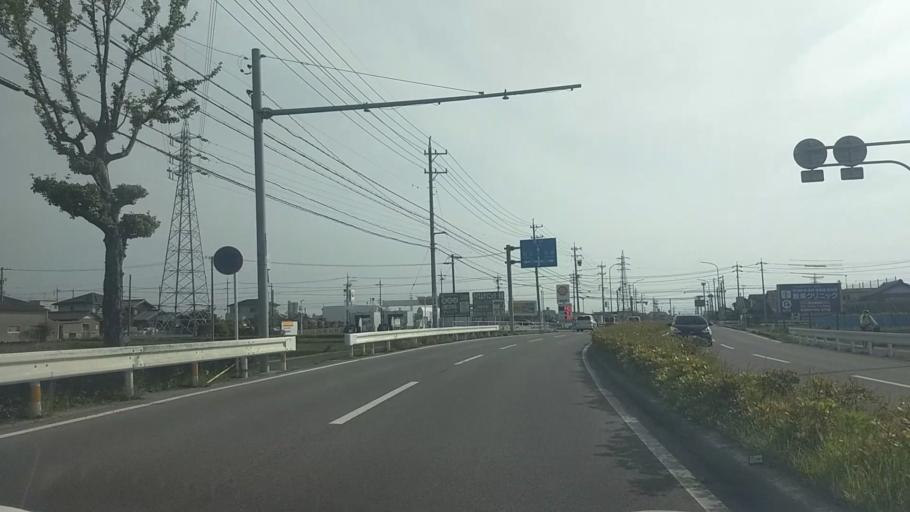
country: JP
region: Aichi
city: Anjo
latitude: 34.9687
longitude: 137.0740
